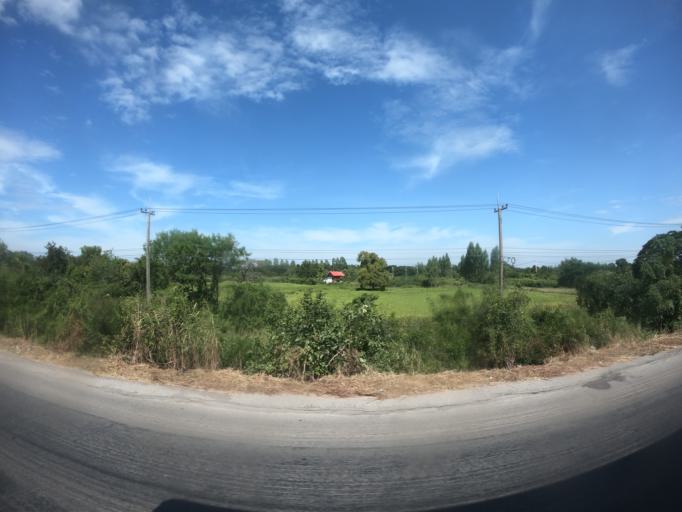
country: TH
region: Khon Kaen
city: Khon Kaen
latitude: 16.4173
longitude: 102.9122
